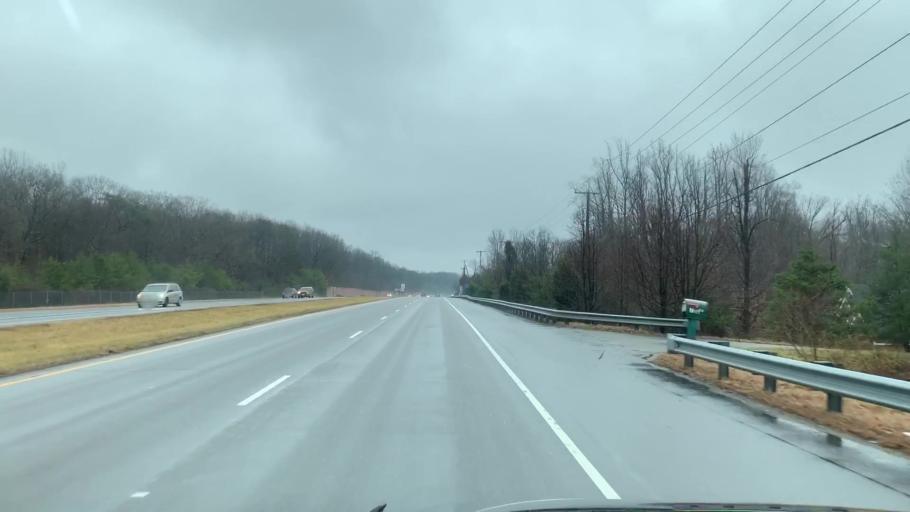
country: US
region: Virginia
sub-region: Fairfax County
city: Burke
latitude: 38.7527
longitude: -77.3011
